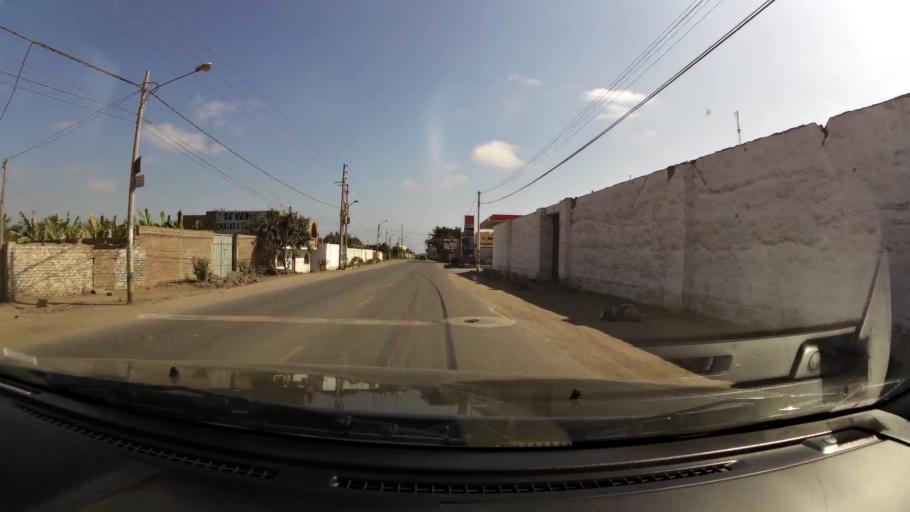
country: PE
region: Ica
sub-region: Provincia de Chincha
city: Sunampe
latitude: -13.4164
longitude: -76.1556
